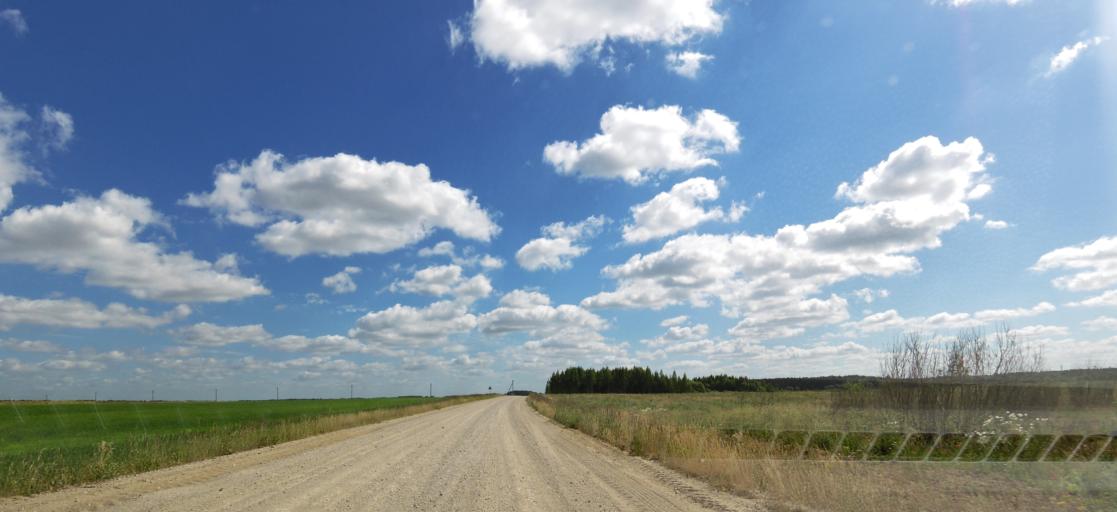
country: LT
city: Vabalninkas
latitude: 56.0250
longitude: 24.8934
